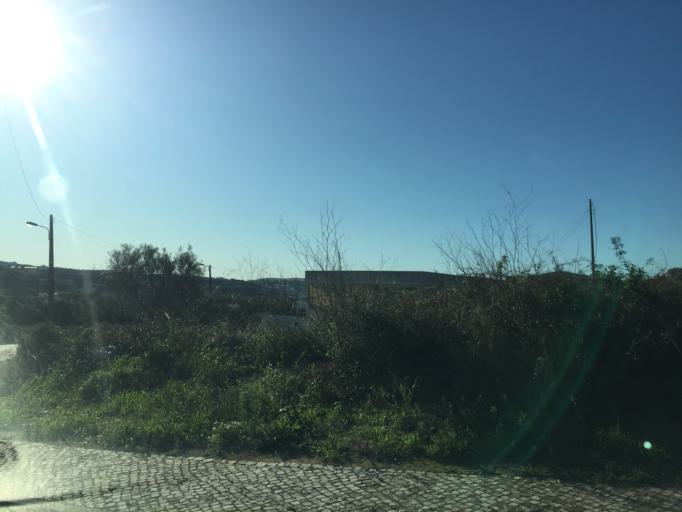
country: PT
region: Lisbon
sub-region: Sintra
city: Pero Pinheiro
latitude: 38.8601
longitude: -9.3218
